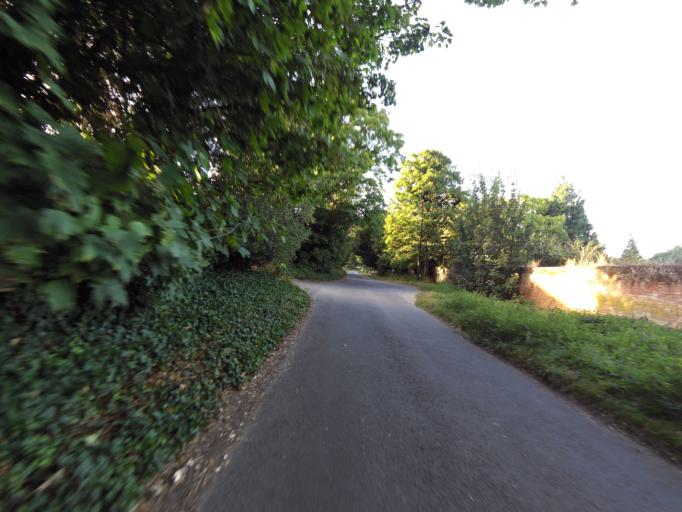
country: GB
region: England
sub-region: Suffolk
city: Kesgrave
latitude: 52.0092
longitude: 1.2319
